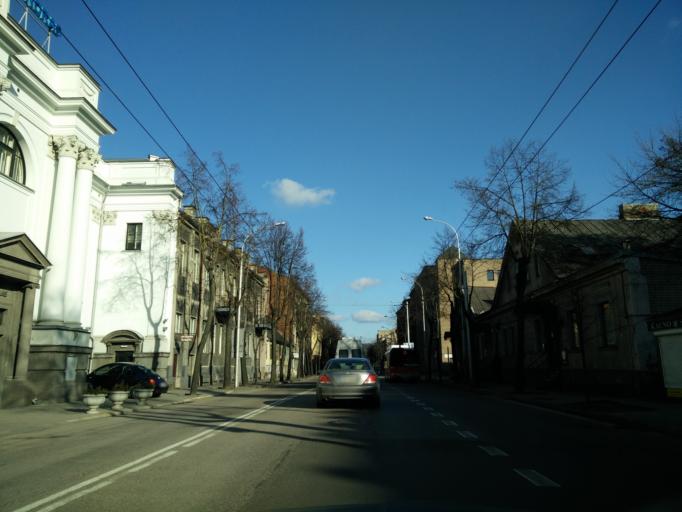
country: LT
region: Kauno apskritis
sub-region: Kaunas
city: Kaunas
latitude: 54.8993
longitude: 23.9071
